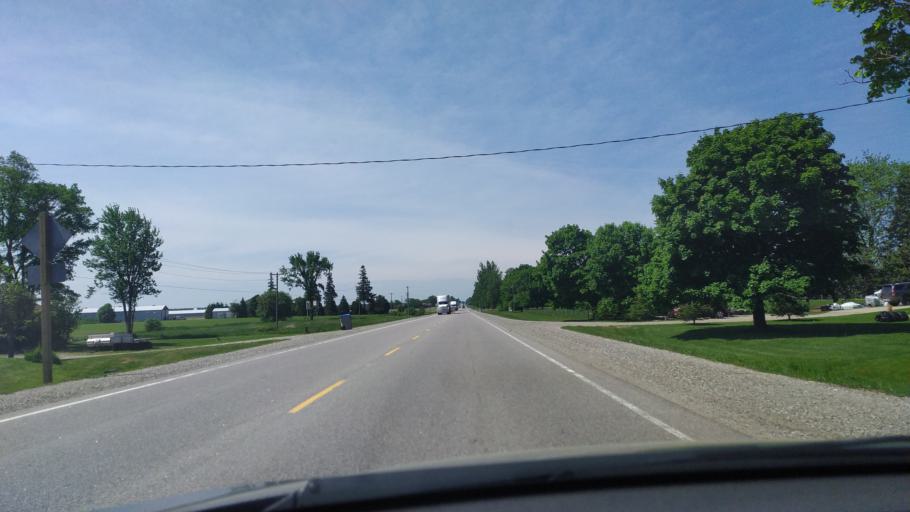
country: CA
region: Ontario
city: Stratford
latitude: 43.3206
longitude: -81.0256
